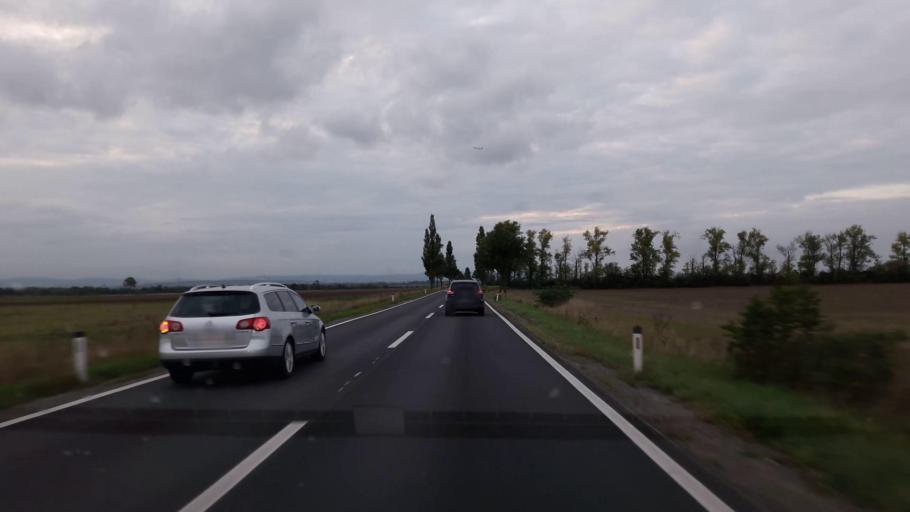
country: AT
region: Lower Austria
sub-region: Politischer Bezirk Wien-Umgebung
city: Rauchenwarth
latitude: 48.1031
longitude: 16.5343
